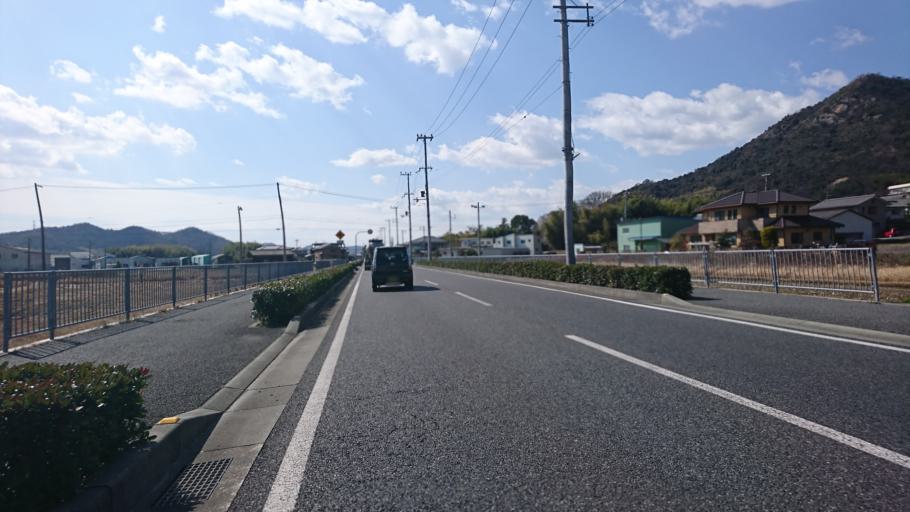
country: JP
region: Hyogo
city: Himeji
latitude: 34.8476
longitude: 134.7516
